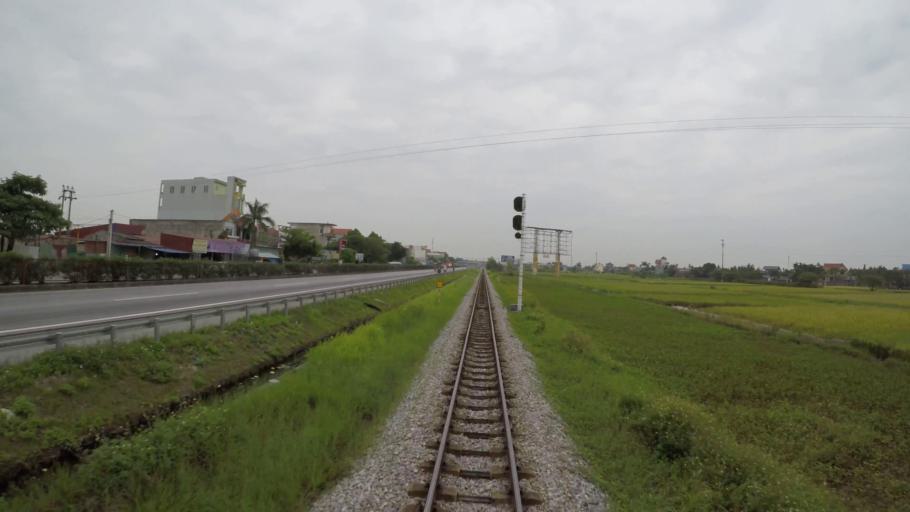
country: VN
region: Hai Duong
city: Phu Thai
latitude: 20.9300
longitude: 106.5542
